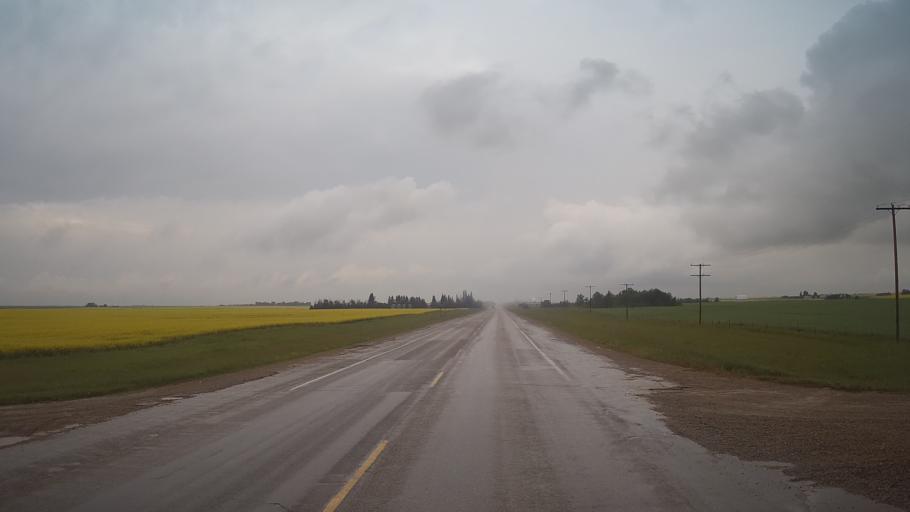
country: CA
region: Saskatchewan
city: Unity
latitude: 52.4349
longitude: -109.0257
